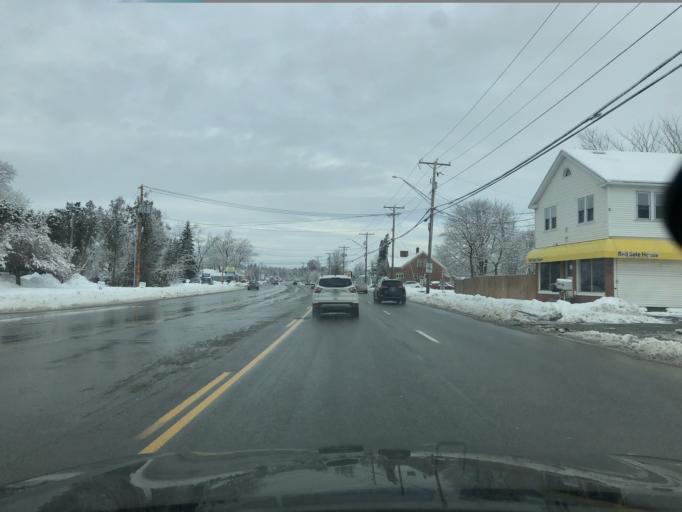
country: US
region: New Hampshire
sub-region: Strafford County
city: Dover
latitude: 43.2311
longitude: -70.8822
